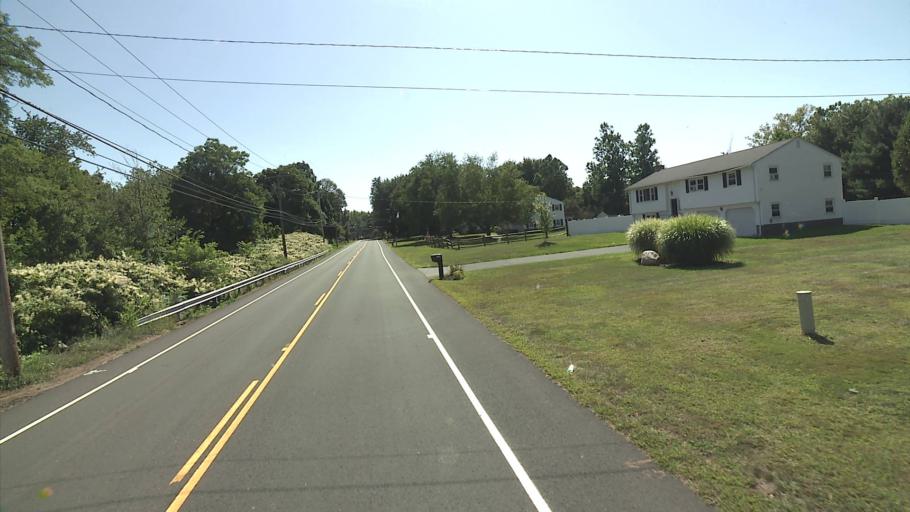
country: US
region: Connecticut
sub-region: Hartford County
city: Windsor Locks
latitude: 41.8908
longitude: -72.6275
